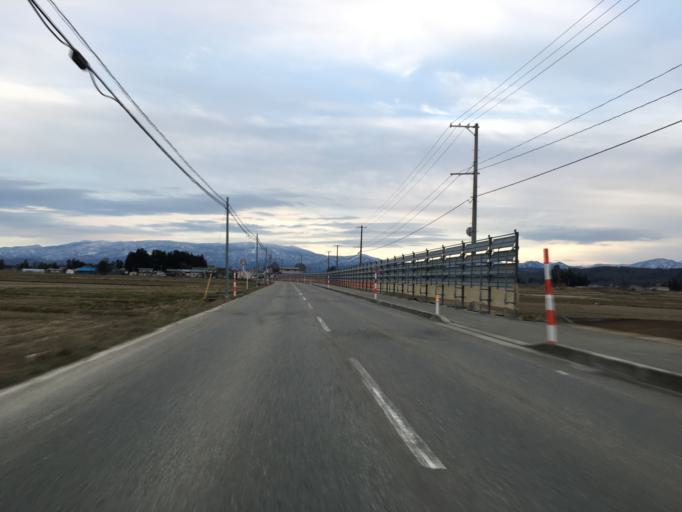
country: JP
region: Yamagata
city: Yonezawa
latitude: 37.9886
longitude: 140.0763
